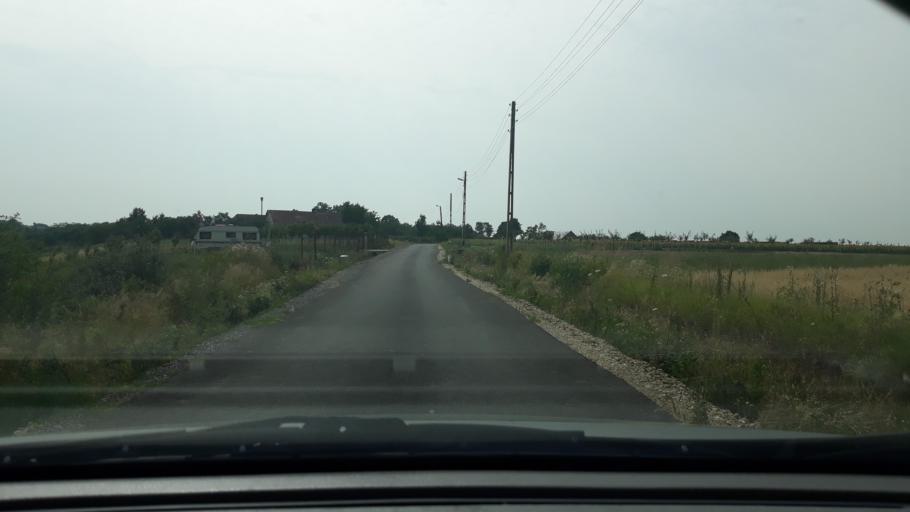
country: RO
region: Bihor
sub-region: Comuna Tauteu
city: Tauteu
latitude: 47.2663
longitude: 22.3097
